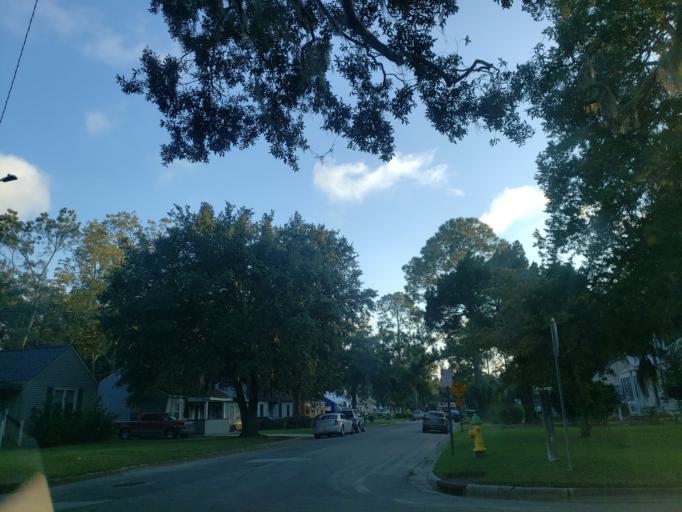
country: US
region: Georgia
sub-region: Chatham County
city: Thunderbolt
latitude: 32.0476
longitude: -81.0750
